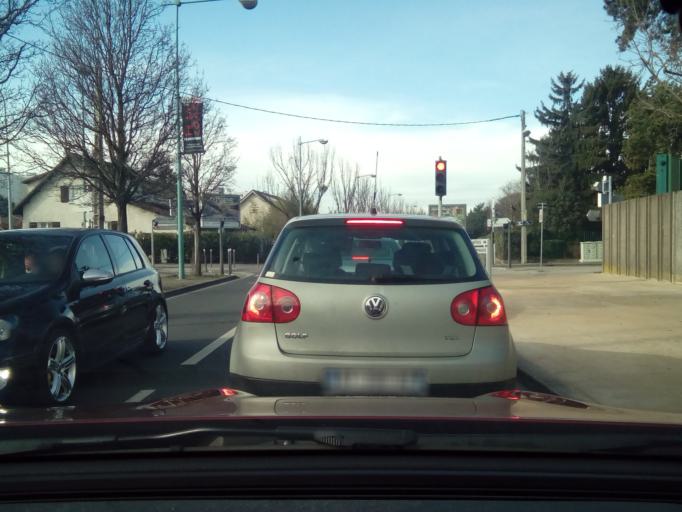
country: FR
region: Rhone-Alpes
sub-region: Departement du Rhone
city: Vaulx-en-Velin
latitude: 45.7871
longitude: 4.9182
